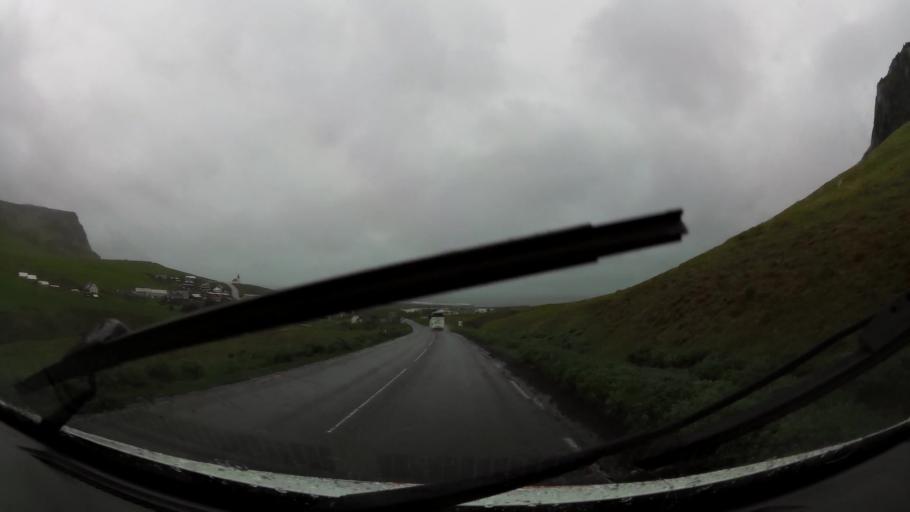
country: IS
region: South
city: Vestmannaeyjar
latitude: 63.4237
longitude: -19.0170
